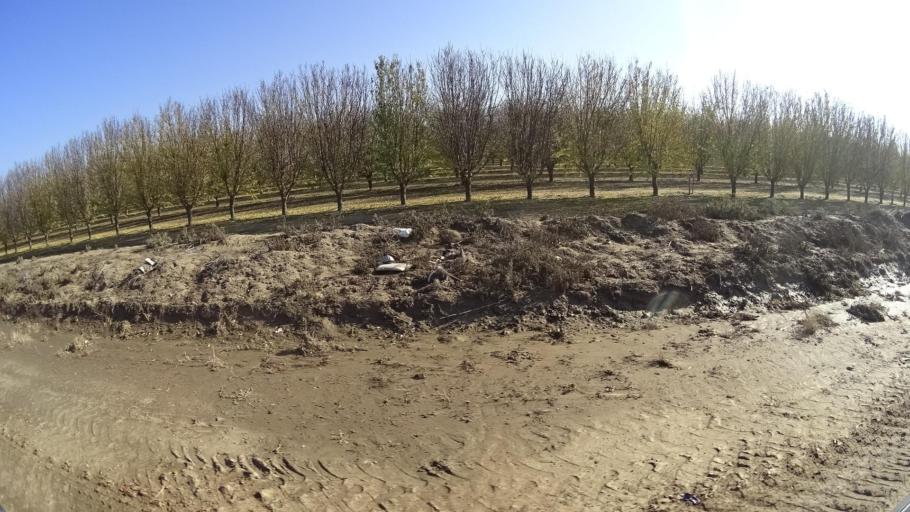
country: US
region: California
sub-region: Kern County
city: Arvin
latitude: 35.1822
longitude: -118.8781
